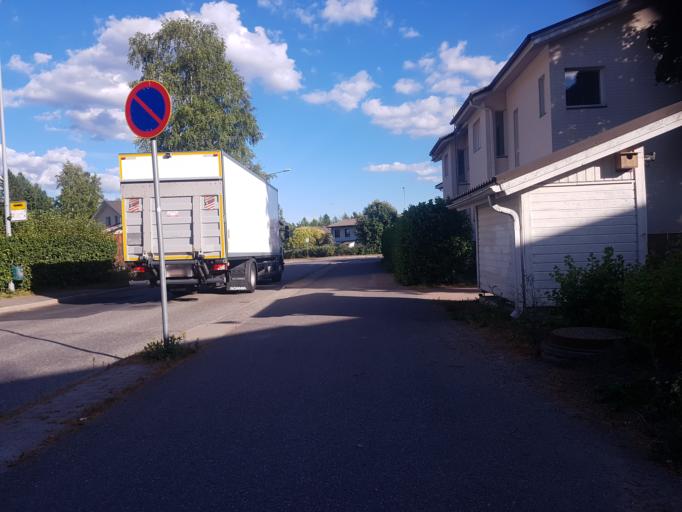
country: FI
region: Uusimaa
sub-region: Helsinki
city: Vantaa
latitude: 60.2695
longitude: 25.0092
